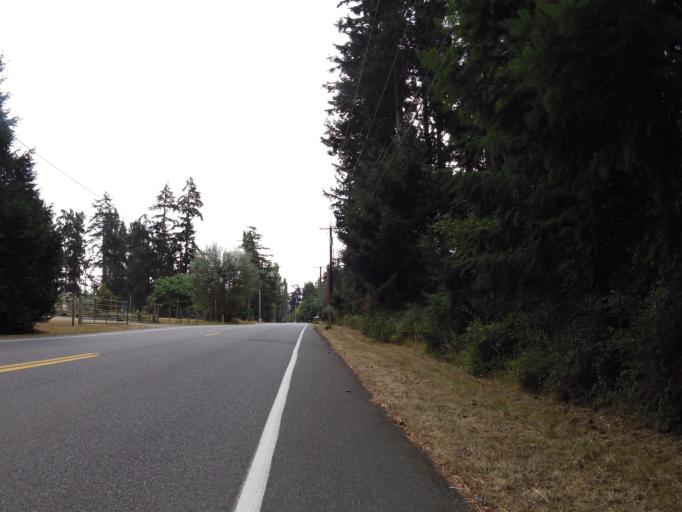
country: US
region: Washington
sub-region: Island County
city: Coupeville
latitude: 48.2012
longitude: -122.6707
